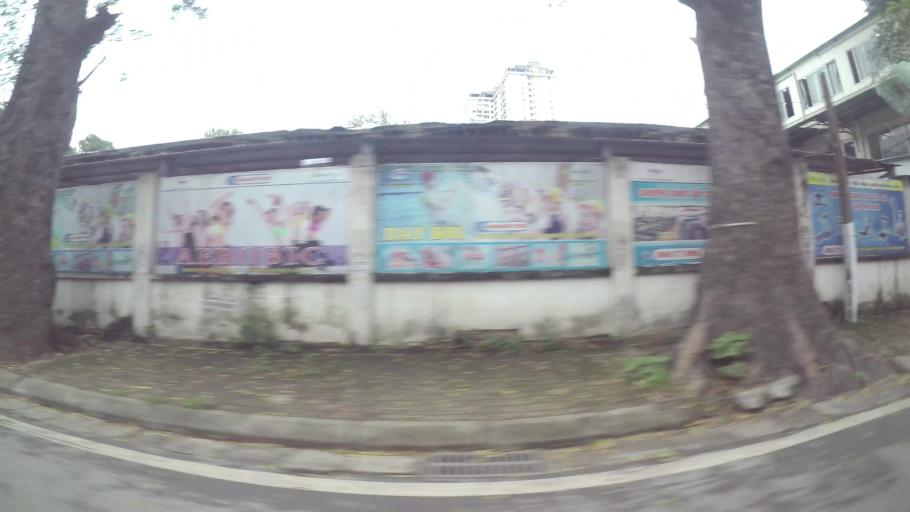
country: VN
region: Ha Noi
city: Hai BaTrung
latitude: 21.0155
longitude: 105.8595
